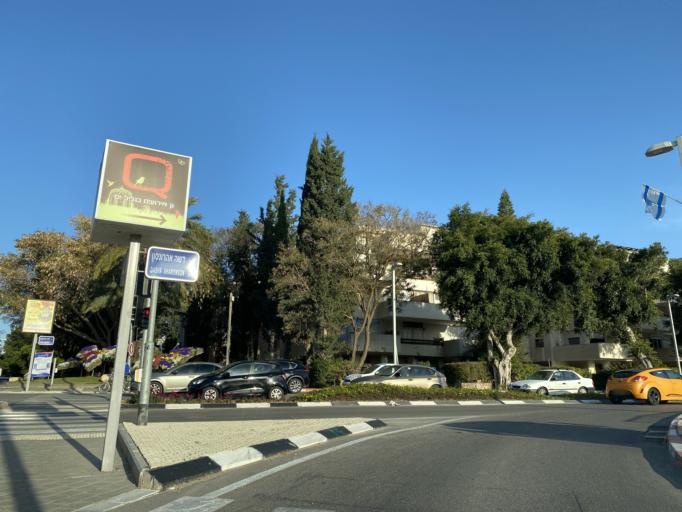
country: IL
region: Tel Aviv
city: Herzliyya
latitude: 32.1624
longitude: 34.8344
